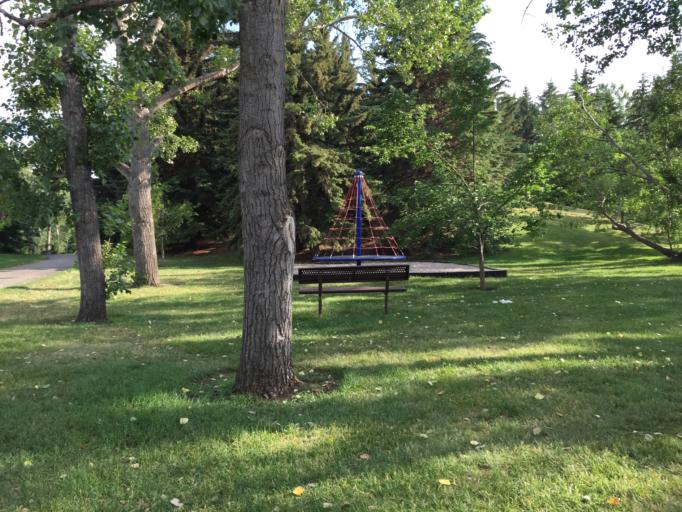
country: CA
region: Alberta
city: Calgary
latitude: 50.9415
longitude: -114.0488
